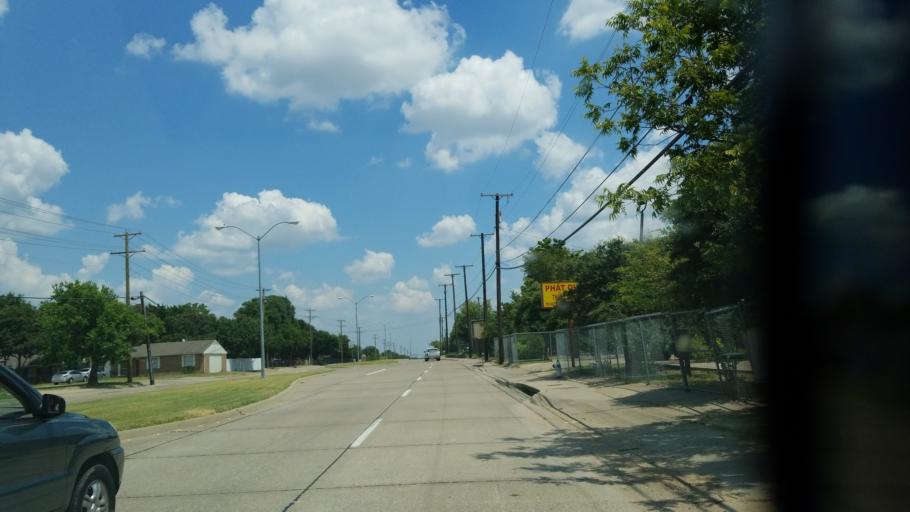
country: US
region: Texas
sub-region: Dallas County
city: Duncanville
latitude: 32.6764
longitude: -96.9011
